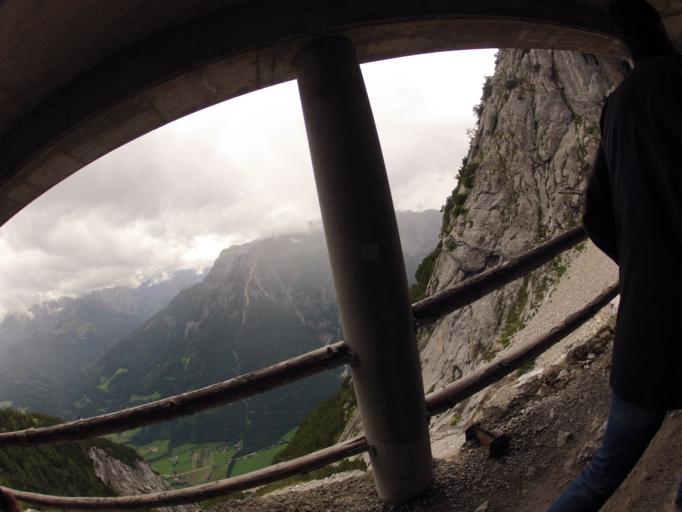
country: AT
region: Salzburg
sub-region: Politischer Bezirk Sankt Johann im Pongau
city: Werfen
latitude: 47.5107
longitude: 13.1933
